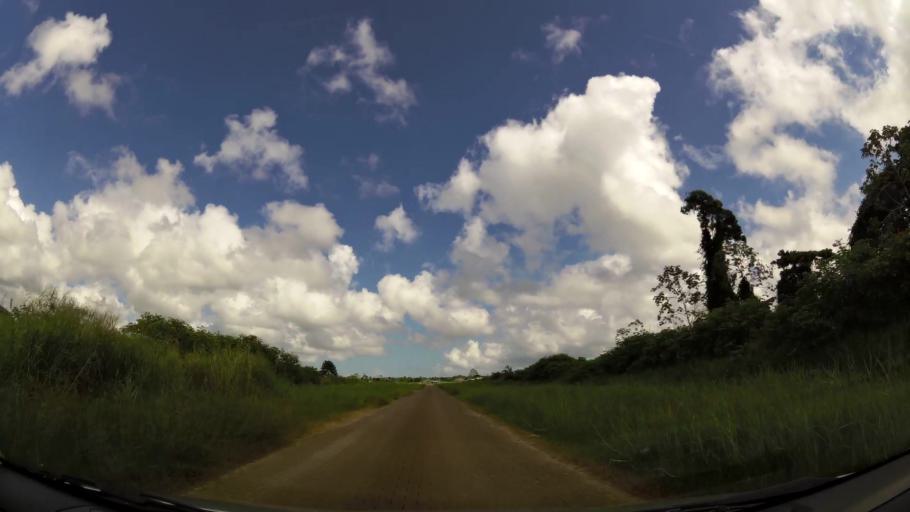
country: SR
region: Paramaribo
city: Paramaribo
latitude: 5.8711
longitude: -55.1286
